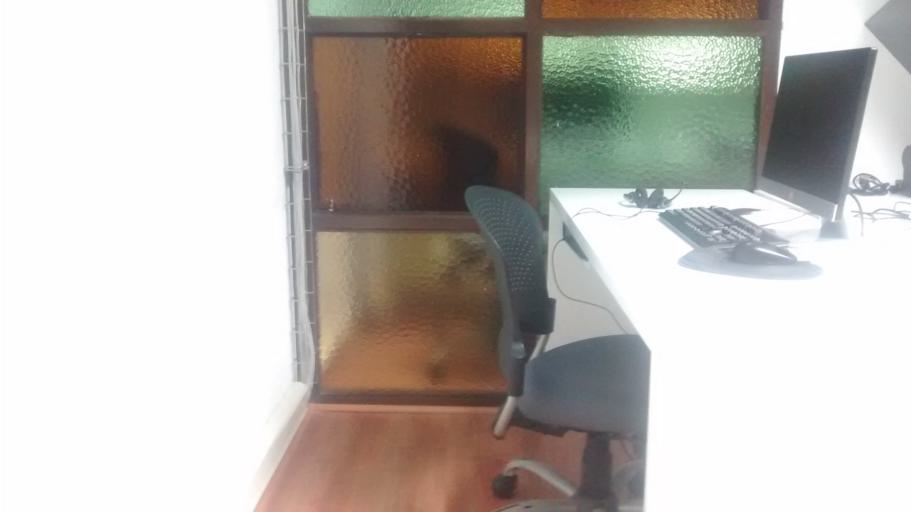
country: MX
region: Jalisco
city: Guadalajara
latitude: 20.6621
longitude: -103.3917
